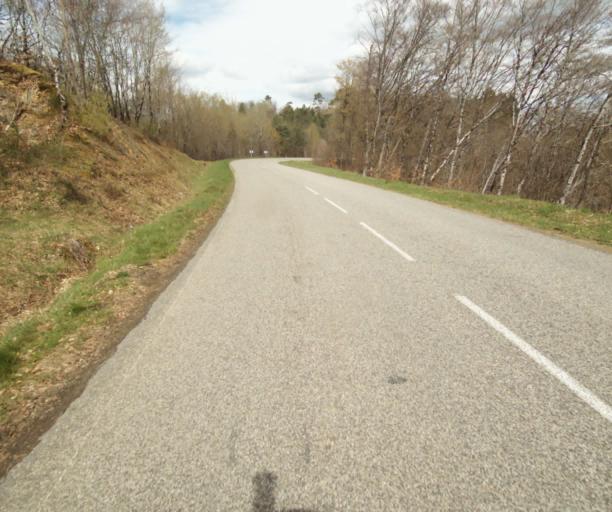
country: FR
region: Limousin
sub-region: Departement de la Correze
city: Laguenne
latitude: 45.2040
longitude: 1.8623
